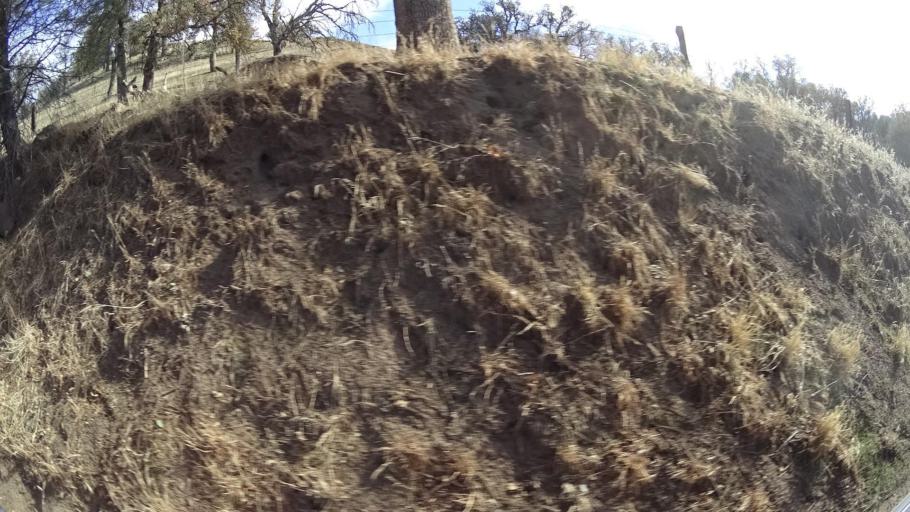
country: US
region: California
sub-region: Kern County
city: Alta Sierra
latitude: 35.6768
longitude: -118.7346
